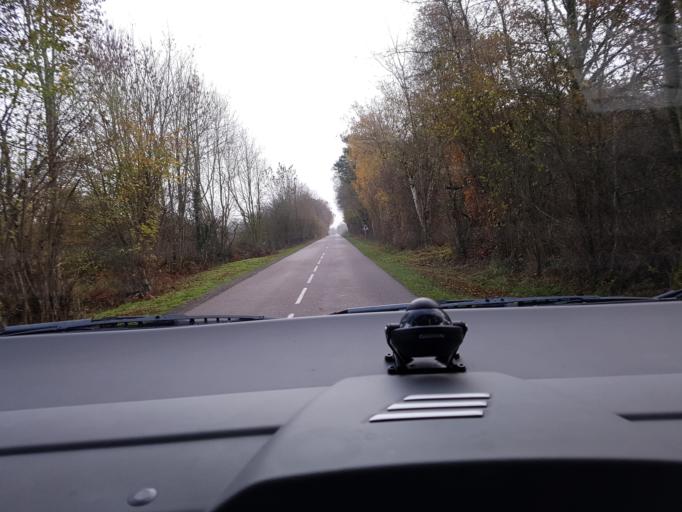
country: FR
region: Lower Normandy
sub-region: Departement de l'Orne
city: Mortree
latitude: 48.6369
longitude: -0.0123
